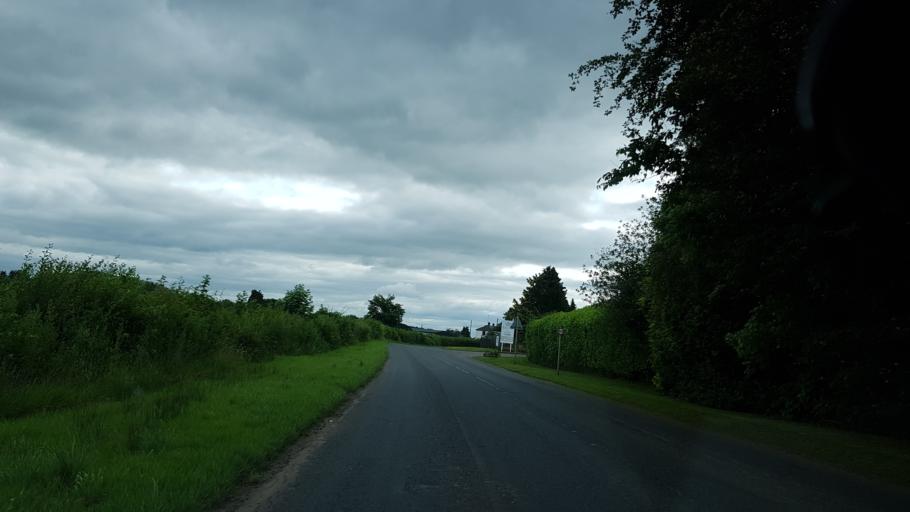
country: GB
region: Wales
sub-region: Monmouthshire
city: Llanarth
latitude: 51.7746
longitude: -2.8897
